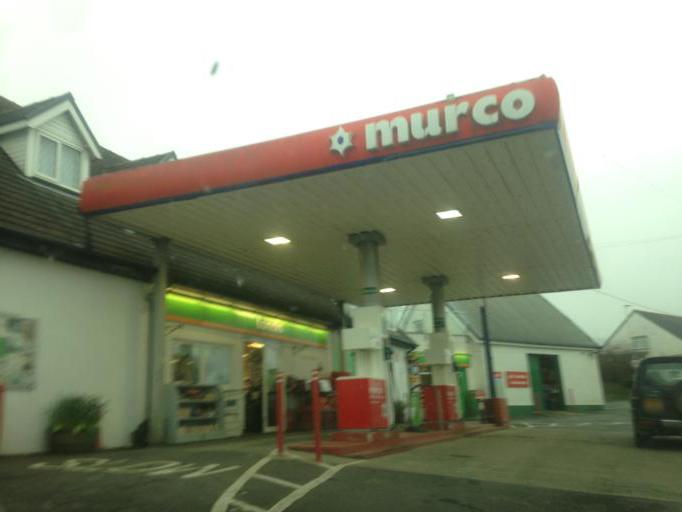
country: GB
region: Wales
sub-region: County of Ceredigion
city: Llanllwchaiarn
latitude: 52.1357
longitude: -4.4377
